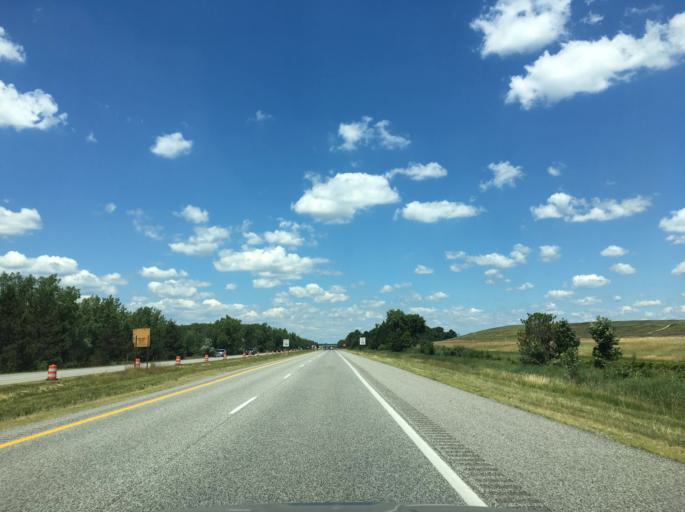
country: US
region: Michigan
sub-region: Midland County
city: Midland
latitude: 43.6277
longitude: -84.1777
